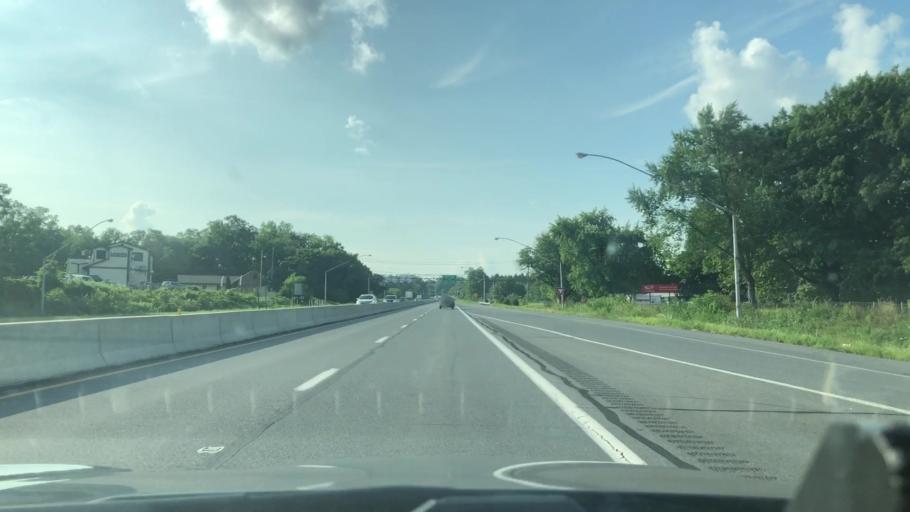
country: US
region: Pennsylvania
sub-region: Lehigh County
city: Wescosville
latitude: 40.6012
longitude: -75.5603
